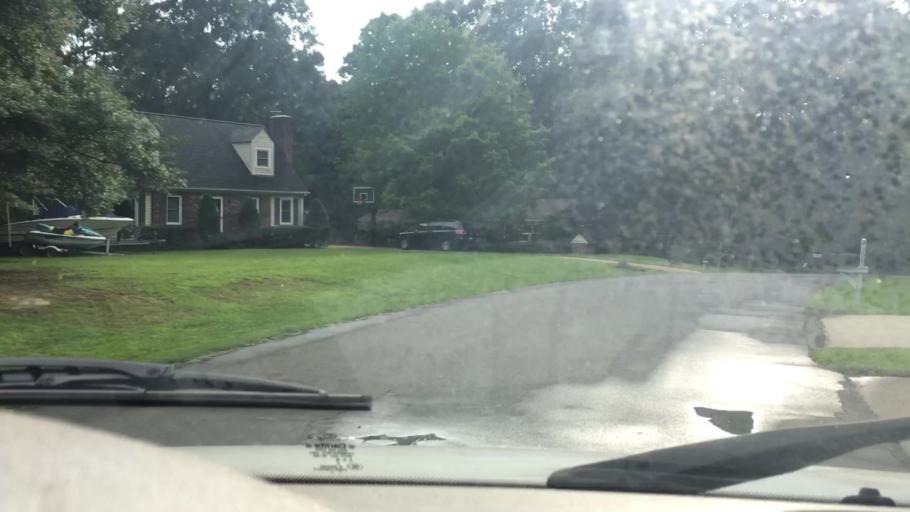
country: US
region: North Carolina
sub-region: Mecklenburg County
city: Cornelius
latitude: 35.4913
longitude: -80.8808
